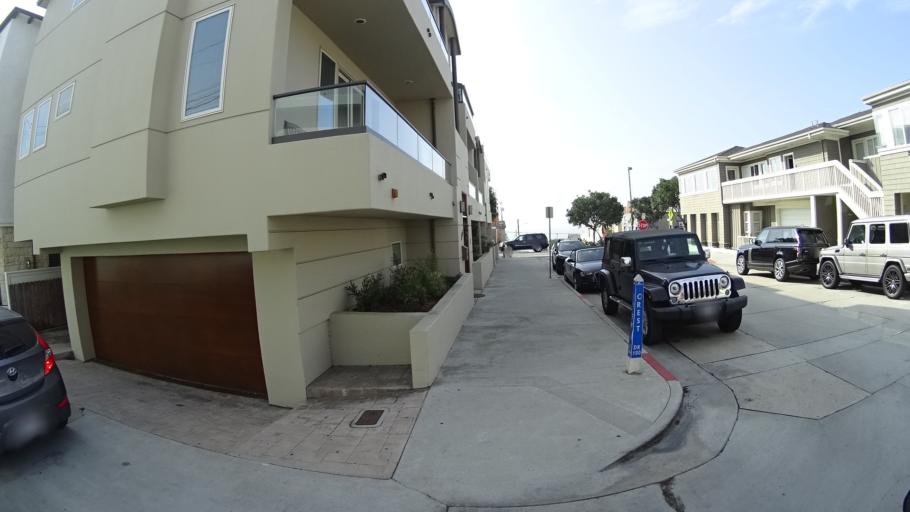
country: US
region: California
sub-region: Los Angeles County
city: Manhattan Beach
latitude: 33.8845
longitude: -118.4089
